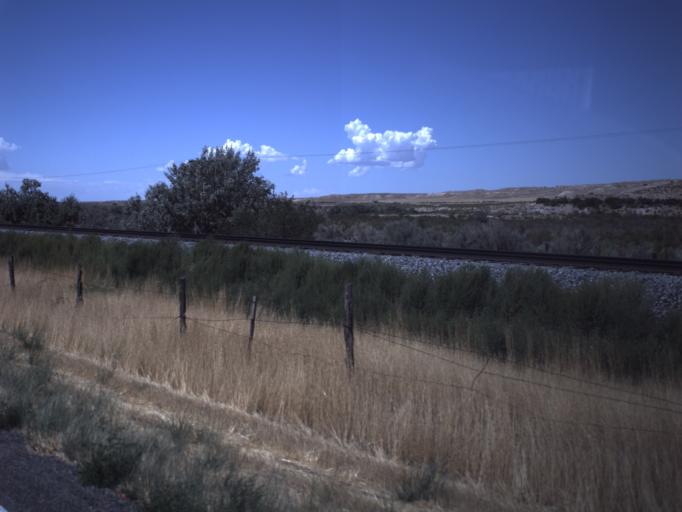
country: US
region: Utah
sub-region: Millard County
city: Delta
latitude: 39.5370
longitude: -112.2662
